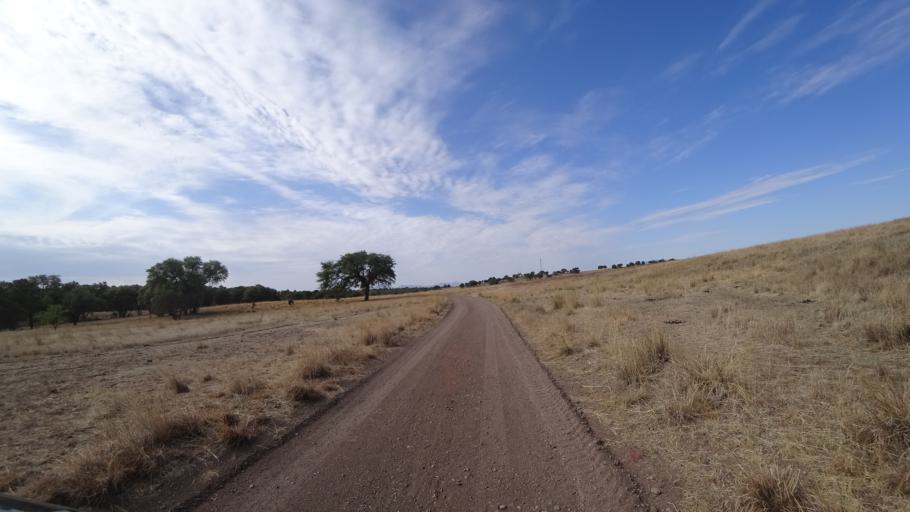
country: MX
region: Sonora
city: Santa Cruz
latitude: 31.4918
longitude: -110.5724
